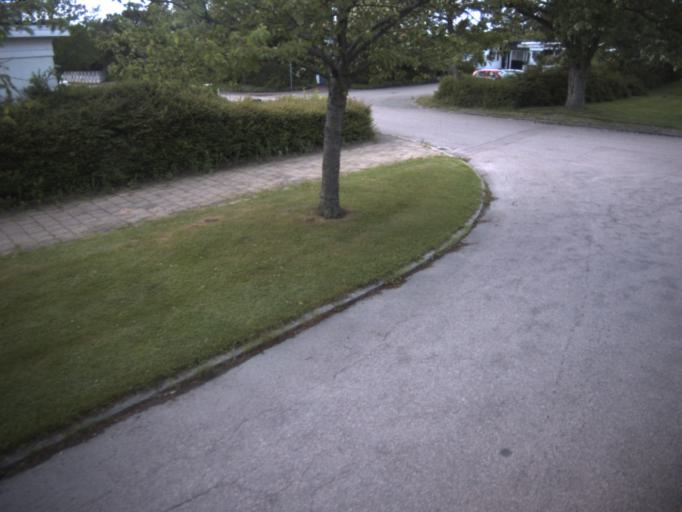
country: SE
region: Skane
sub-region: Helsingborg
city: Helsingborg
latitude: 56.0315
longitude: 12.7432
